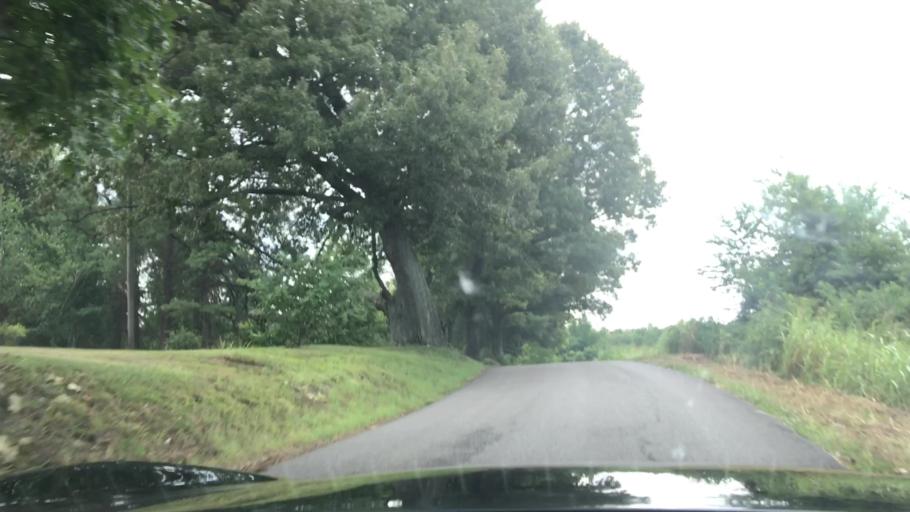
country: US
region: Kentucky
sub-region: Muhlenberg County
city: Central City
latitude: 37.2148
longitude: -87.0468
